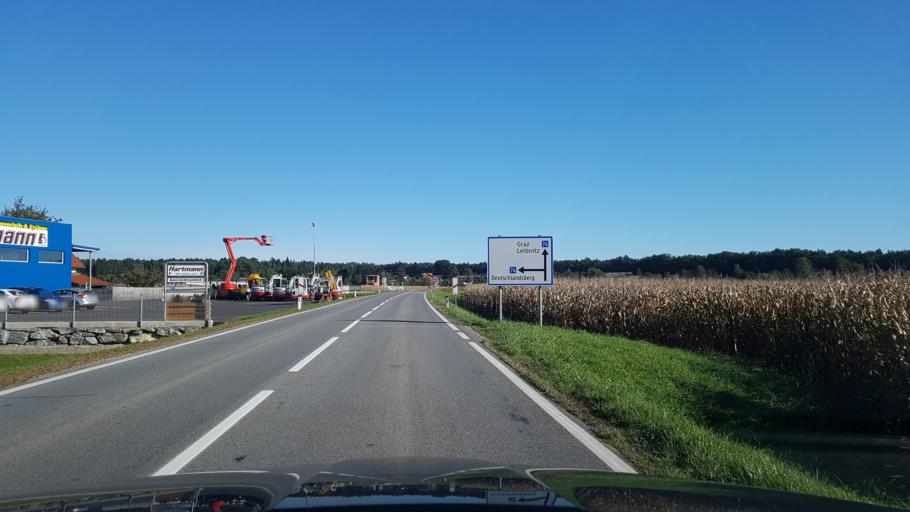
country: AT
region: Styria
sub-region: Politischer Bezirk Leibnitz
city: Gleinstatten
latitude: 46.7498
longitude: 15.3547
